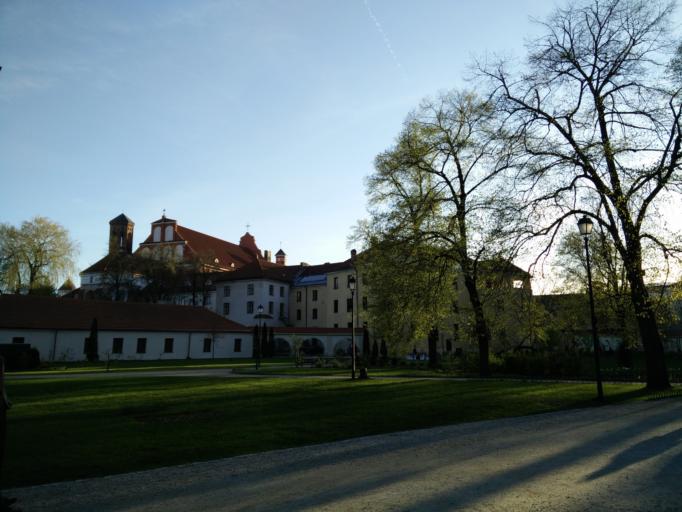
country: LT
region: Vilnius County
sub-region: Vilnius
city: Vilnius
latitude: 54.6842
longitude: 25.2957
